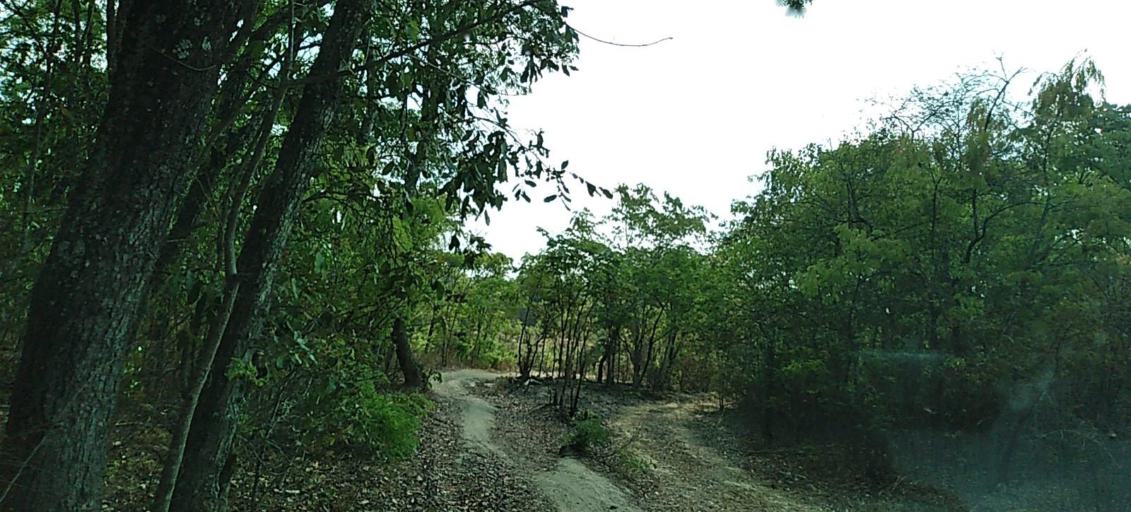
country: ZM
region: Copperbelt
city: Luanshya
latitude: -13.2262
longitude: 28.3331
